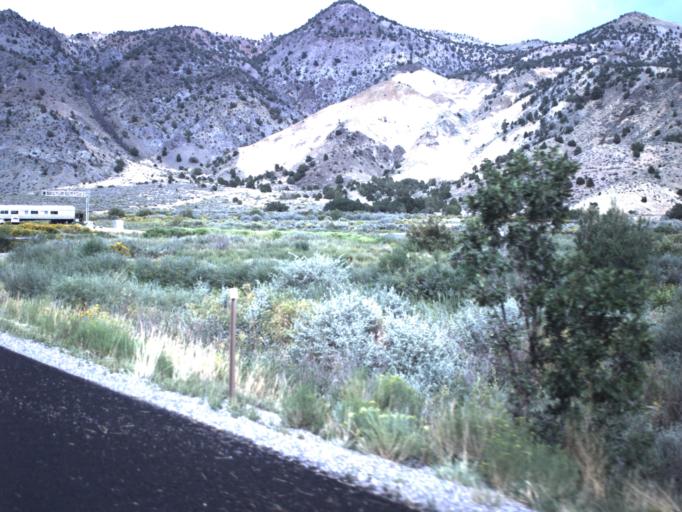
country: US
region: Utah
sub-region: Sevier County
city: Monroe
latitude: 38.5185
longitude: -112.2664
